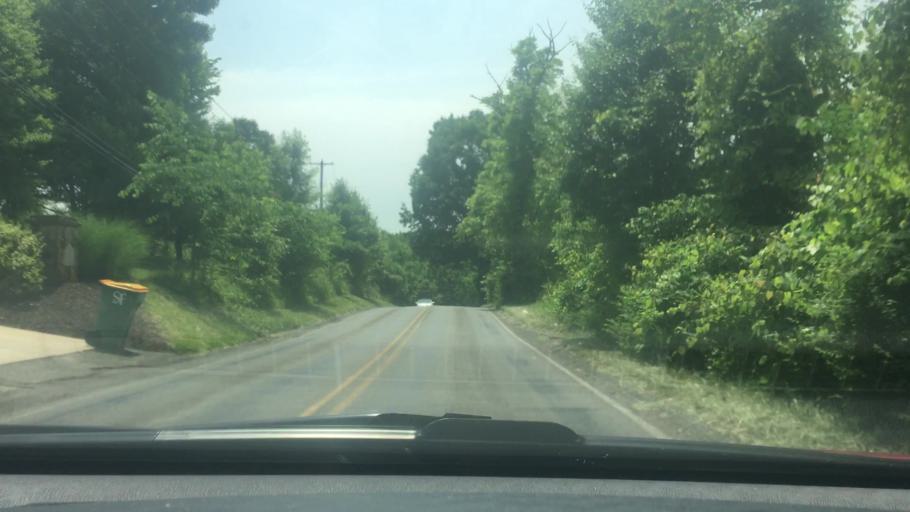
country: US
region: Pennsylvania
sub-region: Allegheny County
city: Bridgeville
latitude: 40.3444
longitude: -80.1493
